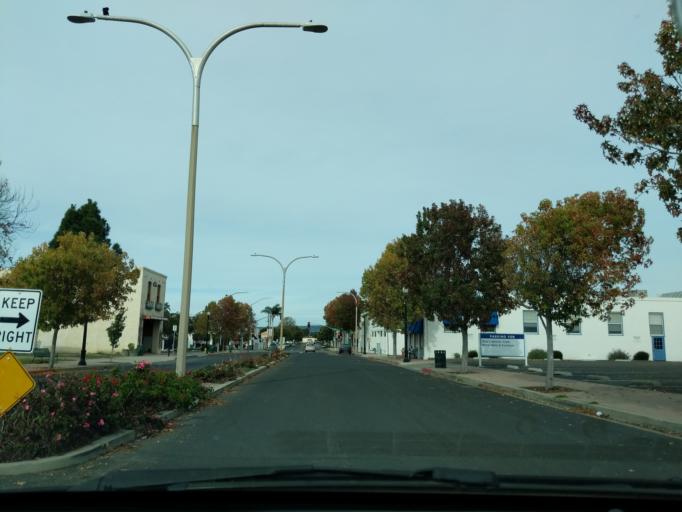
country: US
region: California
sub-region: Santa Barbara County
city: Lompoc
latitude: 34.6377
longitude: -120.4592
